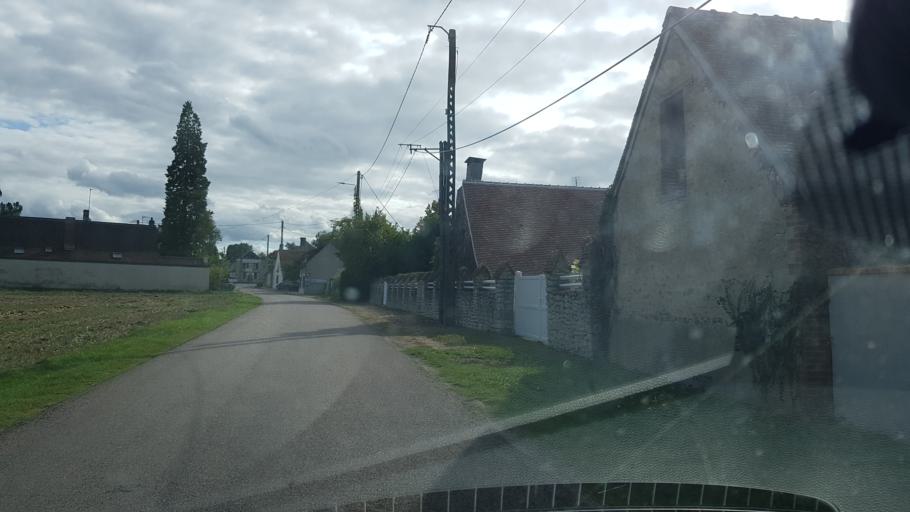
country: FR
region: Centre
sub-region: Departement du Loiret
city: Chilleurs-aux-Bois
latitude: 48.0646
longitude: 2.2139
